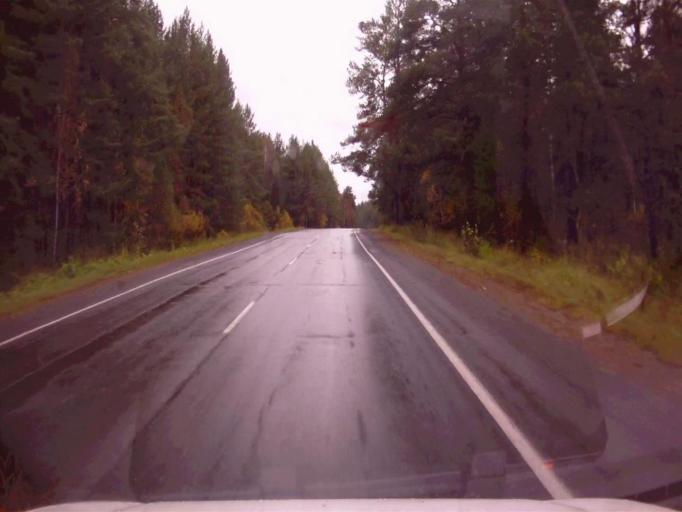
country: RU
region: Chelyabinsk
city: Verkhniy Ufaley
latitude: 56.0212
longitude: 60.3020
